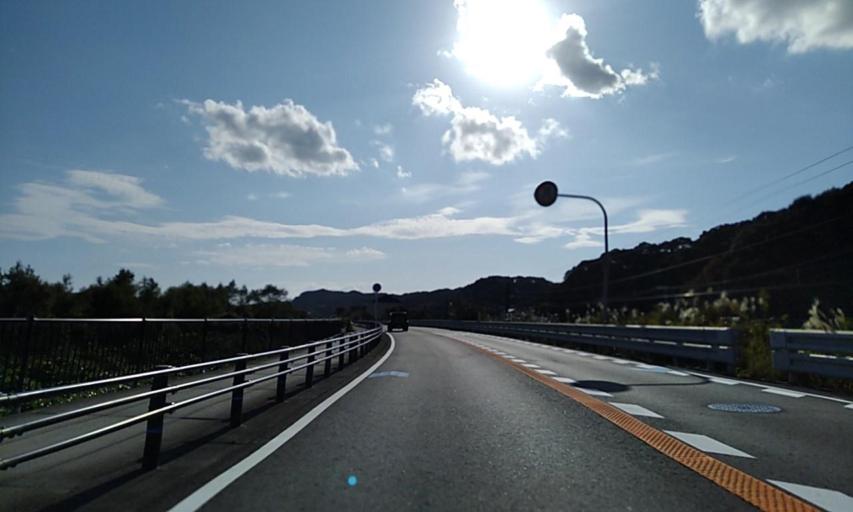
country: JP
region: Wakayama
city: Tanabe
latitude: 33.6853
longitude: 135.4125
